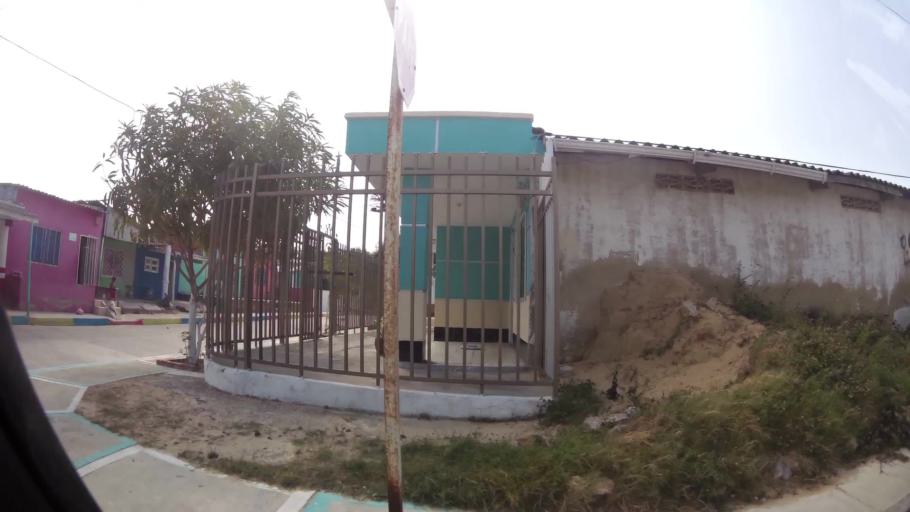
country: CO
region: Atlantico
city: Barranquilla
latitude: 10.9649
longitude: -74.8274
